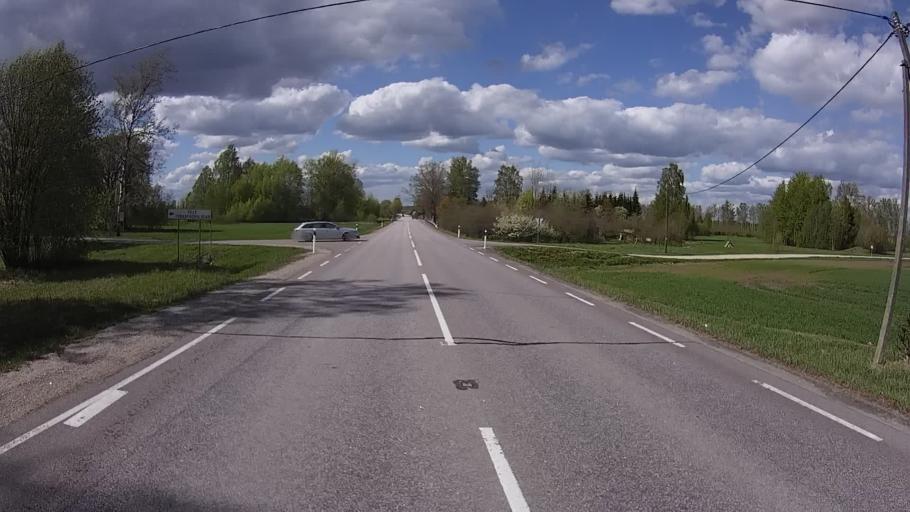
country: EE
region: Jogevamaa
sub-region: Jogeva linn
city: Jogeva
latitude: 58.6738
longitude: 26.4925
